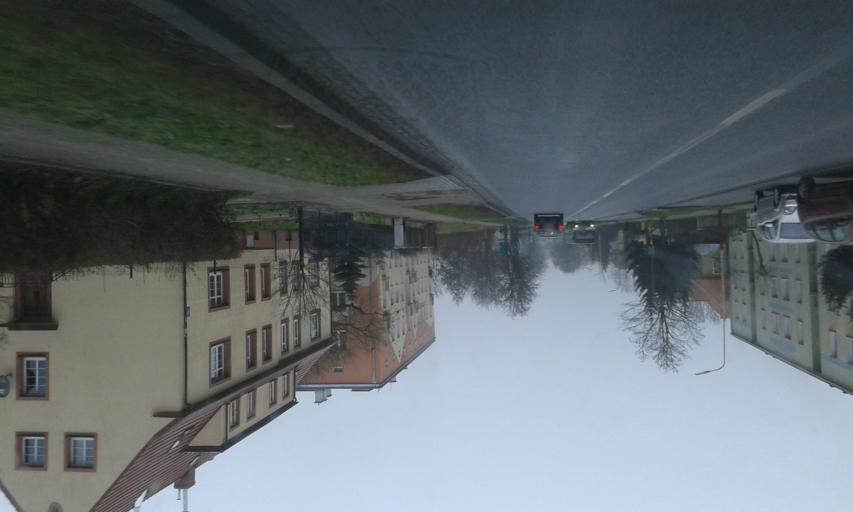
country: PL
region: West Pomeranian Voivodeship
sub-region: Powiat szczecinecki
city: Szczecinek
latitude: 53.6929
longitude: 16.6960
